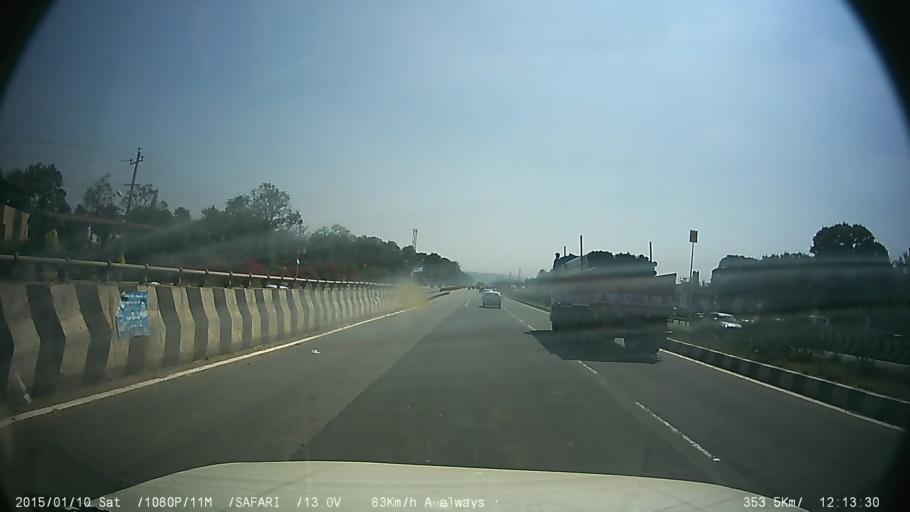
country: IN
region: Karnataka
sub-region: Bangalore Urban
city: Anekal
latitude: 12.8169
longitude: 77.6908
